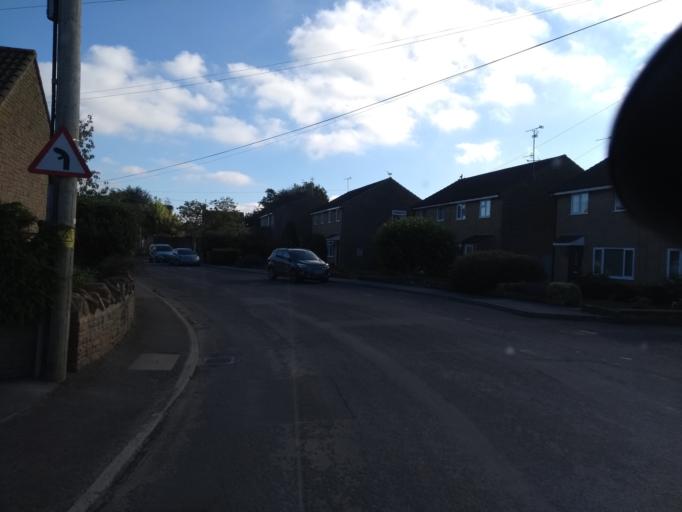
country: GB
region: England
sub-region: Somerset
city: South Petherton
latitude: 50.9462
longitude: -2.8122
